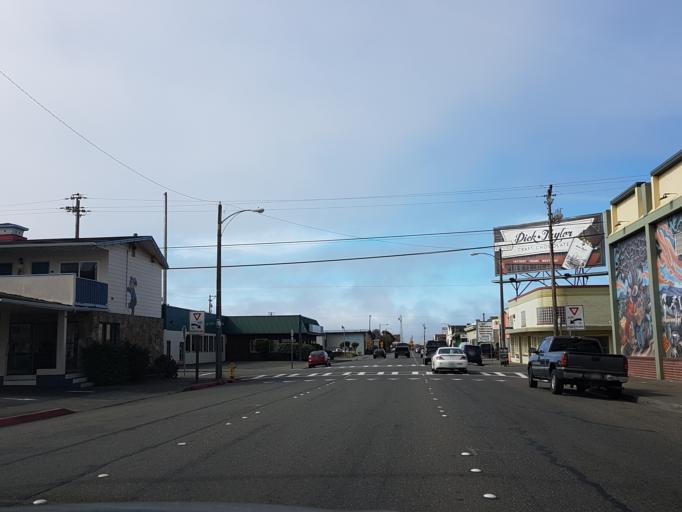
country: US
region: California
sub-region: Humboldt County
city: Eureka
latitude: 40.8021
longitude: -124.1710
